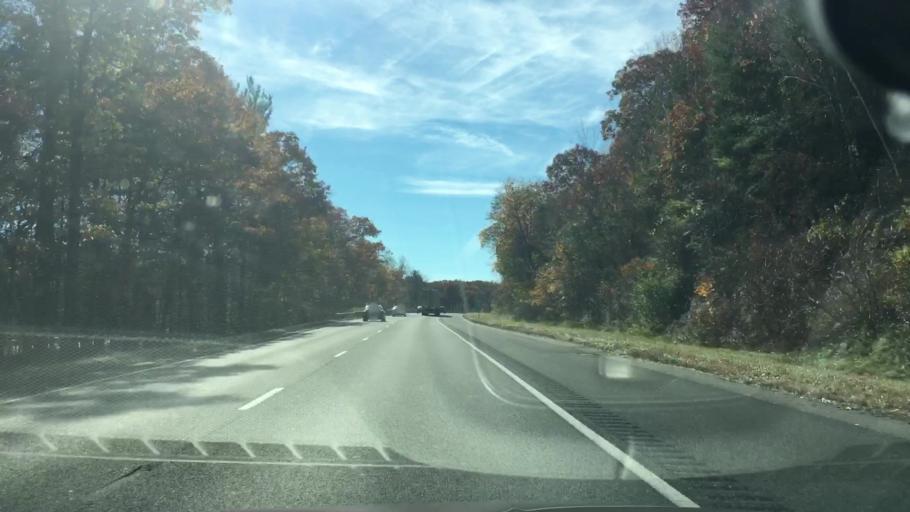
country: US
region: Massachusetts
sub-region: Hampden County
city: Holyoke
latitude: 42.2486
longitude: -72.6244
